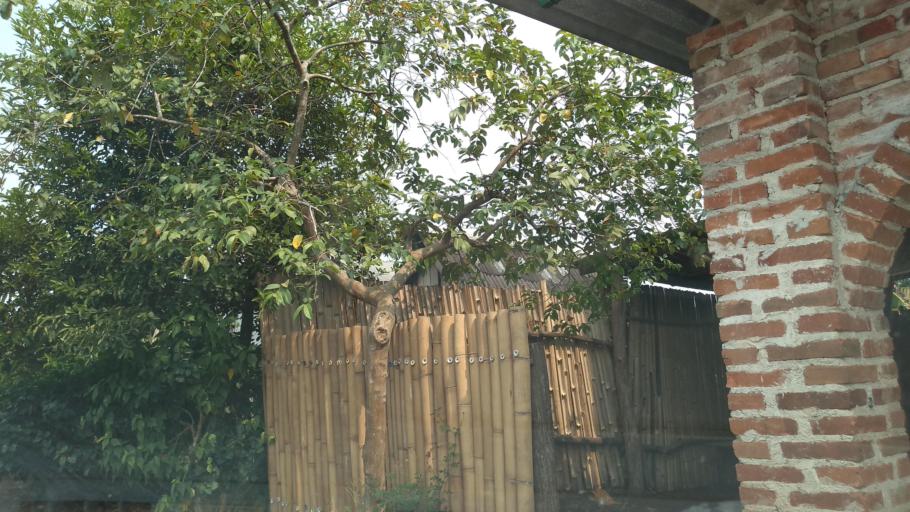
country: MX
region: Veracruz
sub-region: Tezonapa
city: Laguna Chica (Pueblo Nuevo)
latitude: 18.5438
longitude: -96.7620
